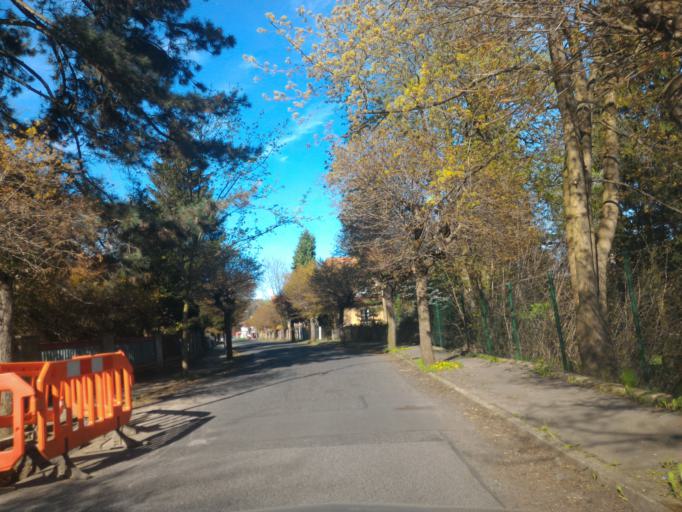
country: CZ
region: Ustecky
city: Varnsdorf
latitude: 50.9072
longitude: 14.6324
